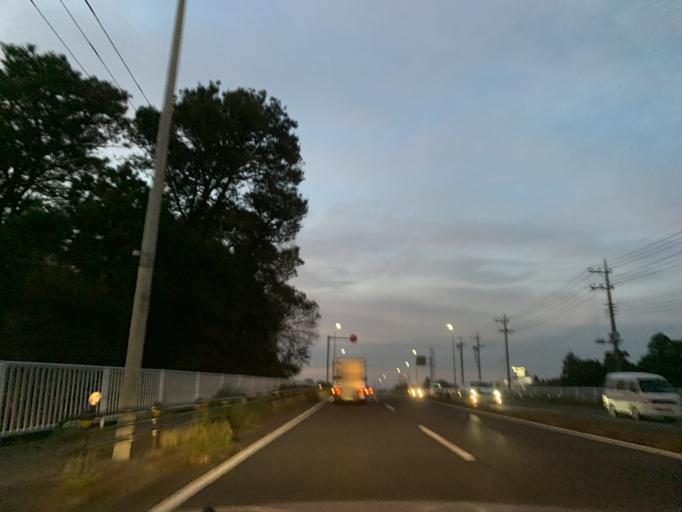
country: JP
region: Chiba
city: Nagareyama
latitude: 35.9155
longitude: 139.9283
